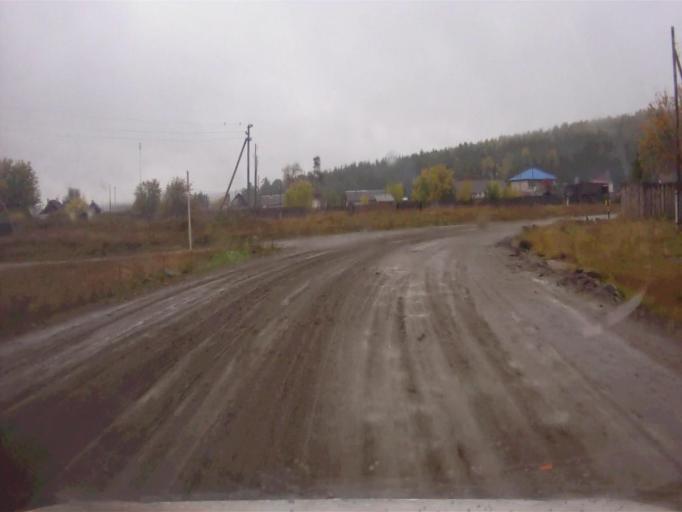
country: RU
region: Chelyabinsk
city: Kyshtym
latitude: 55.9024
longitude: 60.4658
